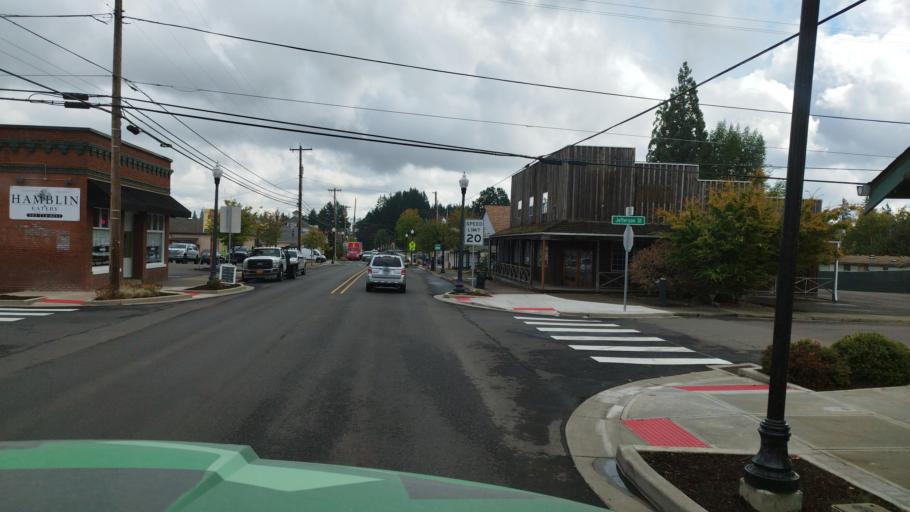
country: US
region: Oregon
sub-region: Yamhill County
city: Lafayette
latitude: 45.2440
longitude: -123.1145
